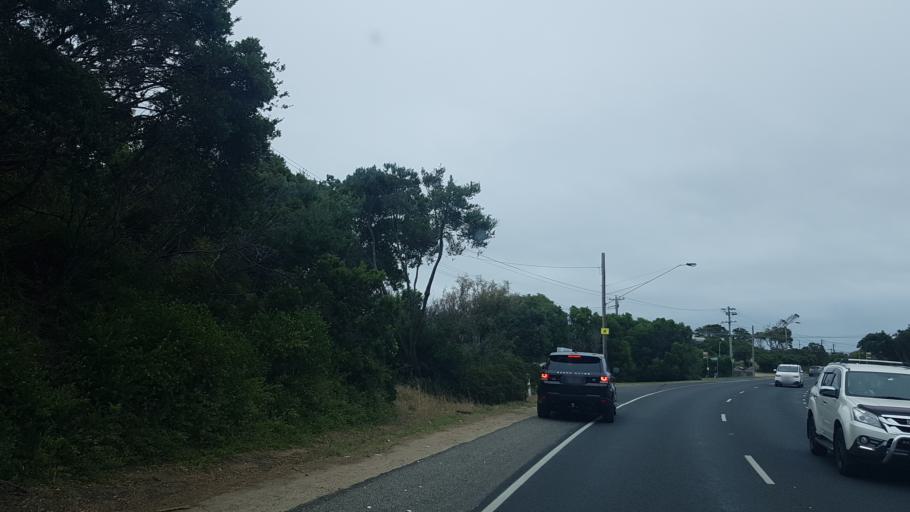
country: AU
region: Victoria
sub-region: Mornington Peninsula
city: Sorrento
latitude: -38.3463
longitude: 144.7402
